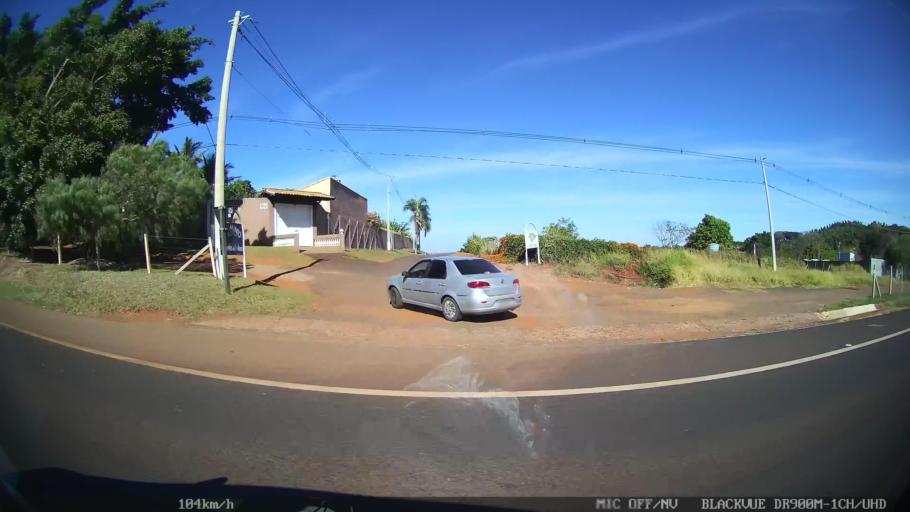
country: BR
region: Sao Paulo
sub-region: Franca
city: Franca
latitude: -20.5805
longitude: -47.3399
